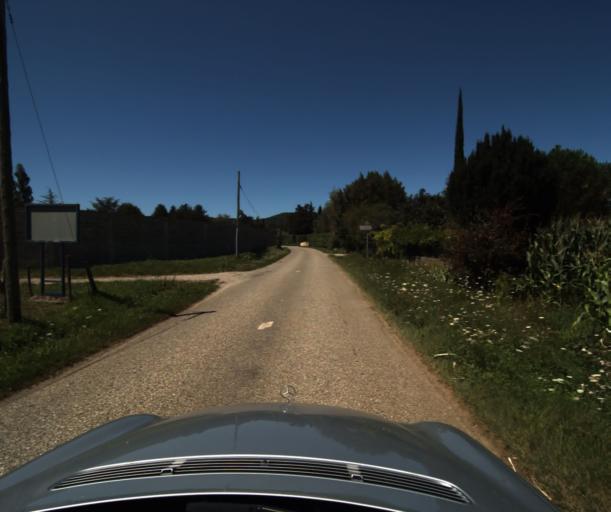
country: FR
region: Midi-Pyrenees
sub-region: Departement de l'Ariege
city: Belesta
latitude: 42.9874
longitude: 1.9189
